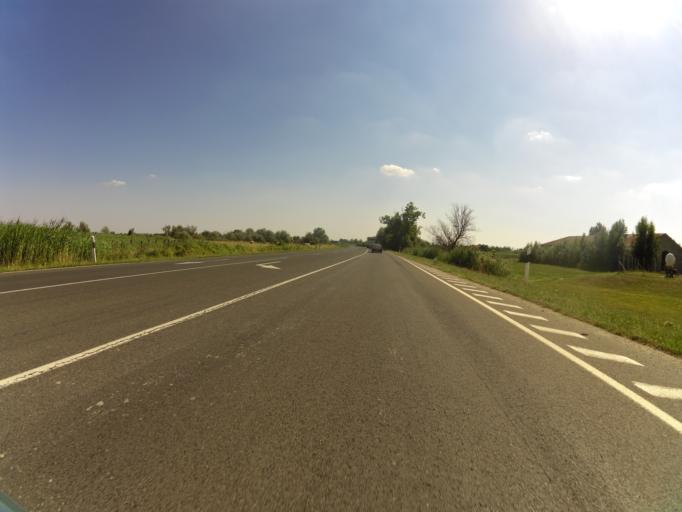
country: HU
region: Csongrad
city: Szatymaz
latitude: 46.3250
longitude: 20.0630
